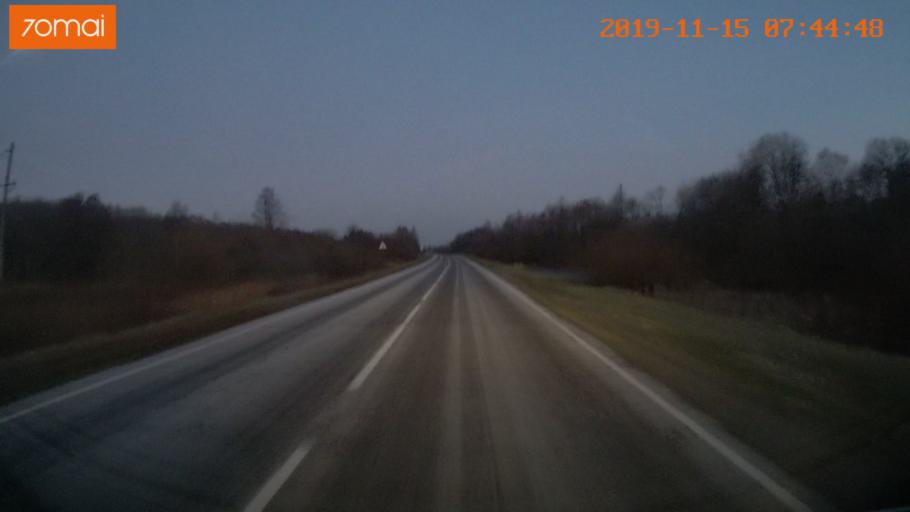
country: RU
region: Vologda
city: Sheksna
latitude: 58.8172
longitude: 38.3078
